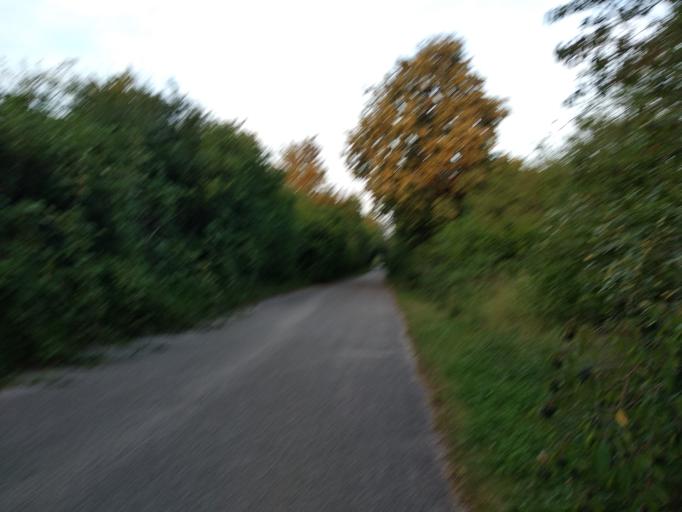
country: DE
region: Bavaria
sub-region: Upper Bavaria
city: Vaterstetten
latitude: 48.1426
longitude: 11.7796
